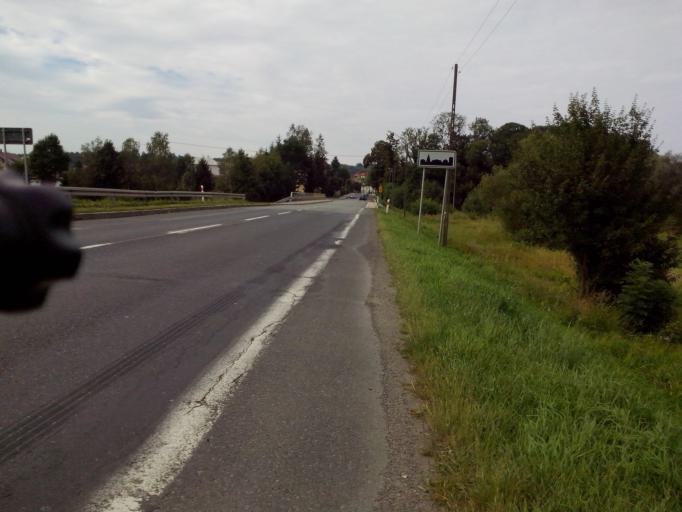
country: PL
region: Subcarpathian Voivodeship
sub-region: Powiat brzozowski
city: Domaradz
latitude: 49.7922
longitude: 21.9469
